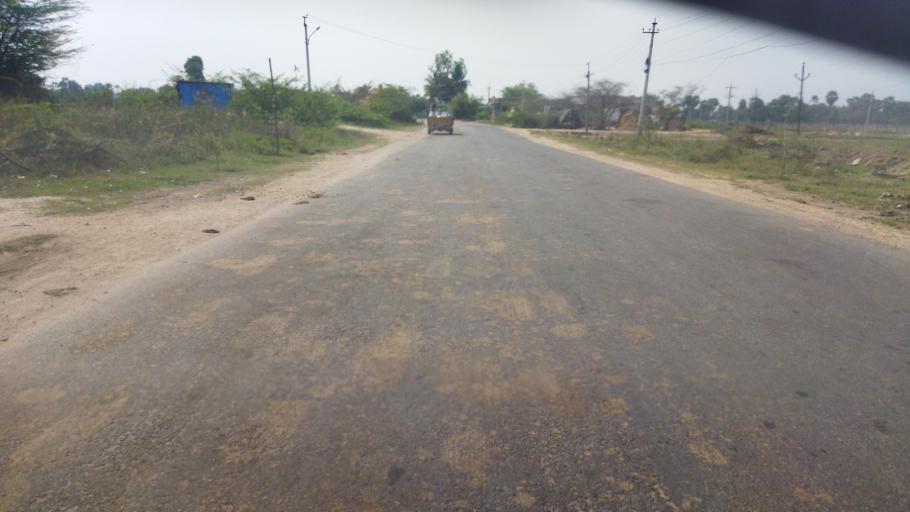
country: IN
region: Telangana
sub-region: Nalgonda
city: Nalgonda
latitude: 17.1527
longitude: 79.3108
